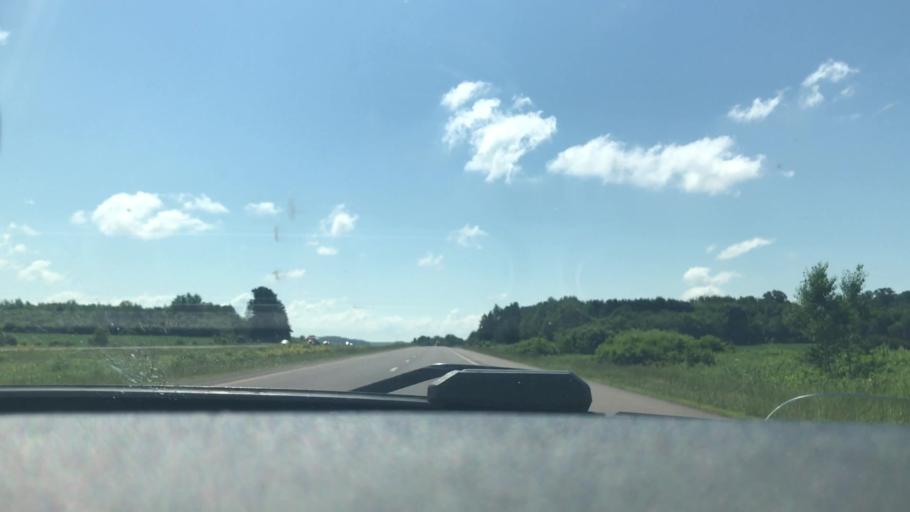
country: US
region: Wisconsin
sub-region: Chippewa County
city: Bloomer
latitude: 45.0790
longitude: -91.4800
